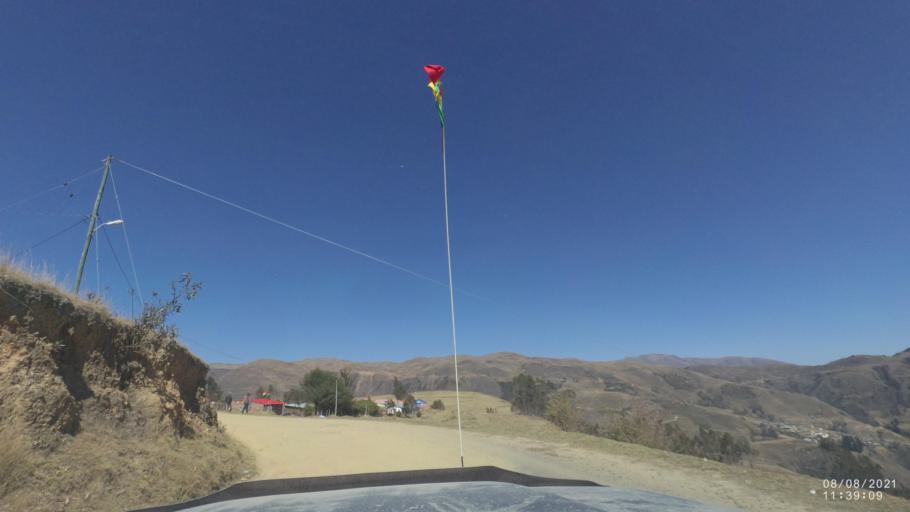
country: BO
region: Cochabamba
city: Colchani
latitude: -16.7932
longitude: -66.6514
